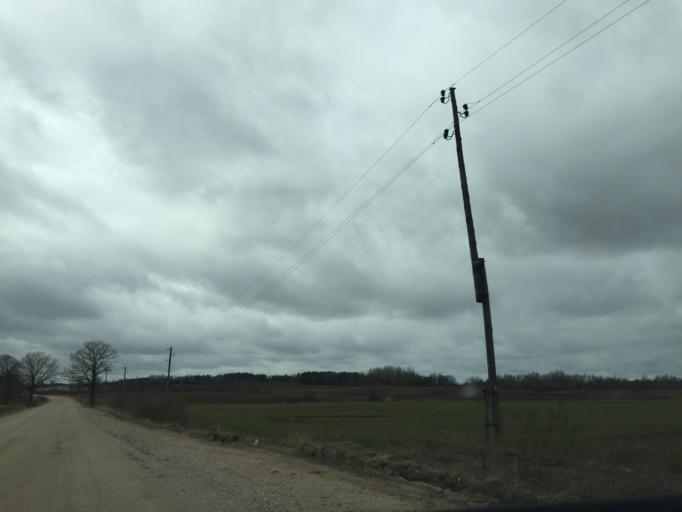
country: LV
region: Aglona
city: Aglona
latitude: 55.9415
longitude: 26.9595
